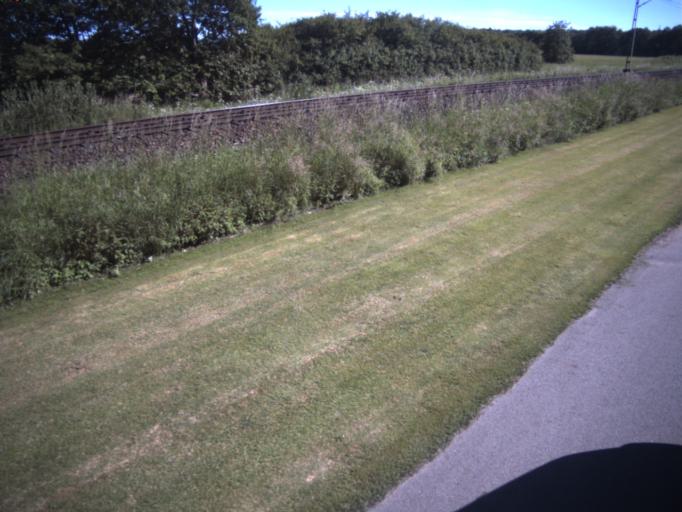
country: SE
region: Skane
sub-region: Helsingborg
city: Odakra
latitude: 56.0984
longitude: 12.7378
